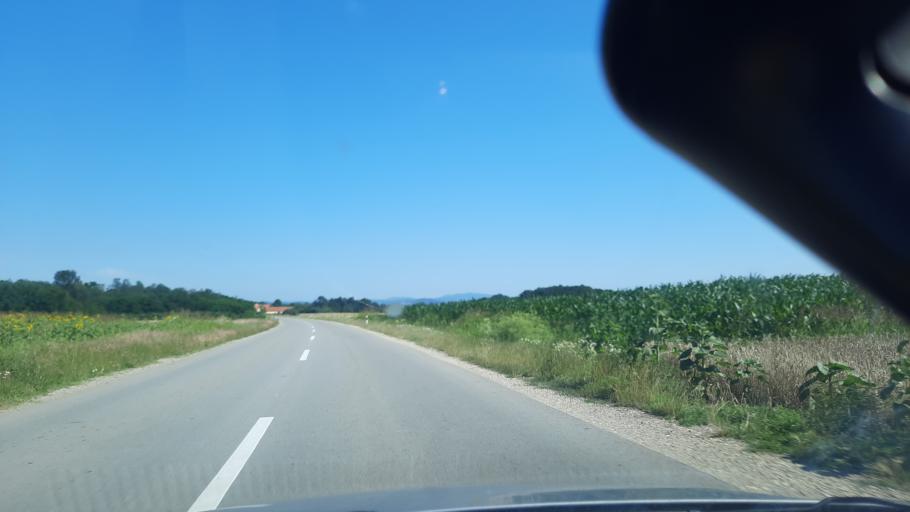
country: RS
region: Central Serbia
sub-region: Branicevski Okrug
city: Malo Crnice
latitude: 44.5605
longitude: 21.4369
